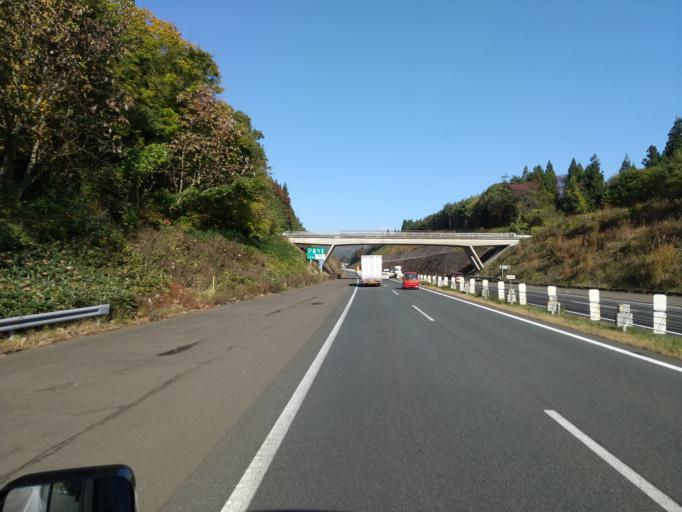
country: JP
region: Iwate
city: Hanamaki
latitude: 39.4920
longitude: 141.1087
